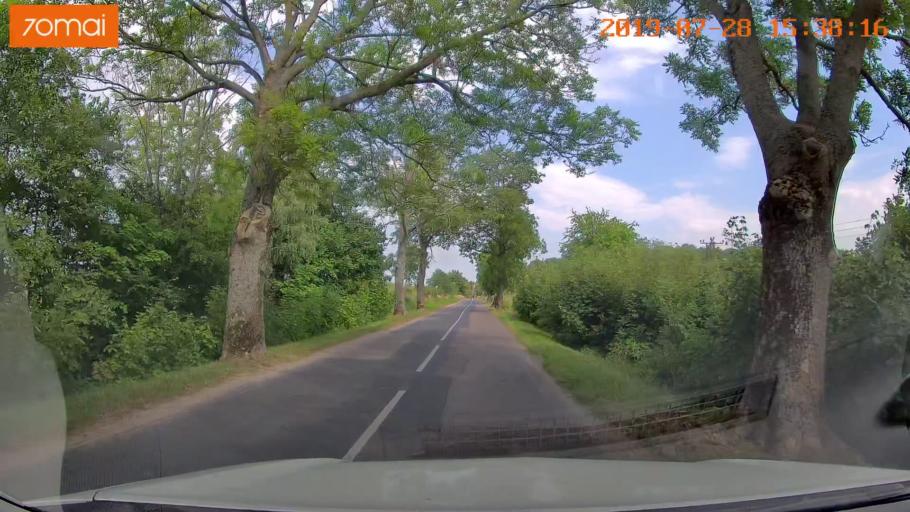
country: RU
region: Kaliningrad
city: Donskoye
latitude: 54.8956
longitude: 20.0139
